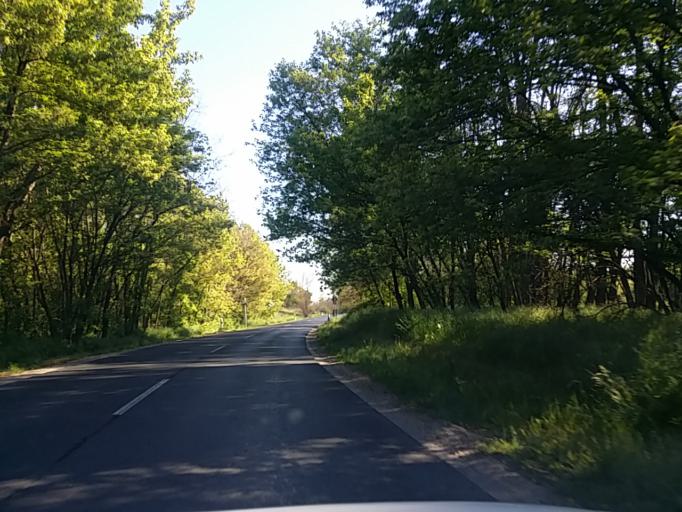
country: HU
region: Pest
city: Fot
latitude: 47.6293
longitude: 19.1995
